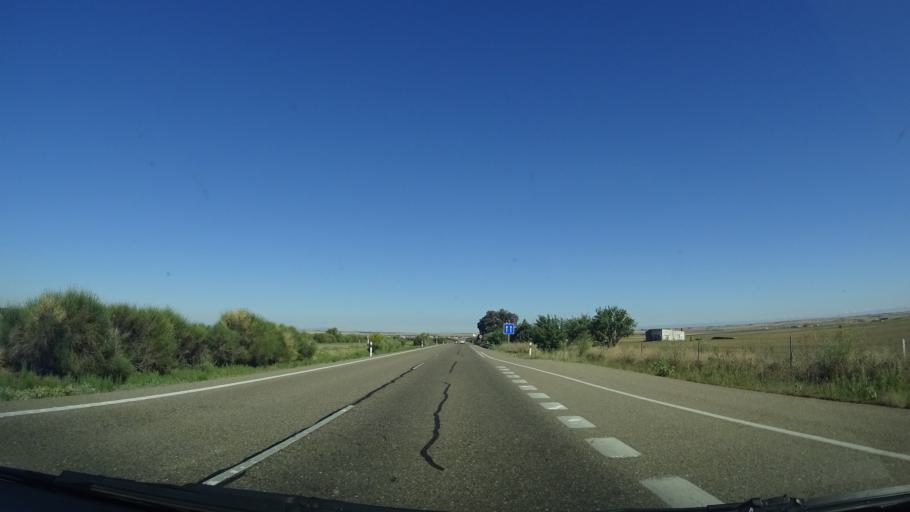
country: ES
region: Castille and Leon
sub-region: Provincia de Zamora
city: Villalpando
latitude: 41.8316
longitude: -5.3823
